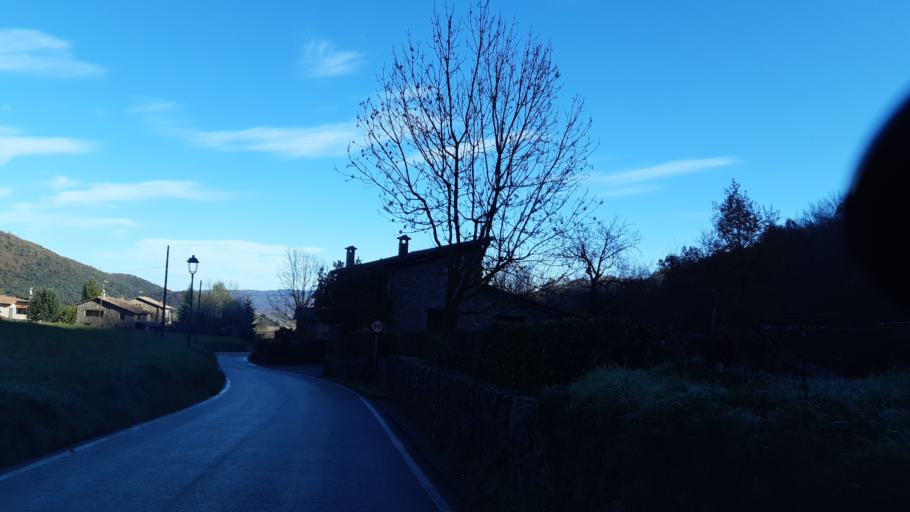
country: ES
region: Catalonia
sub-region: Provincia de Girona
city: Bas
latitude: 42.1492
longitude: 2.4115
